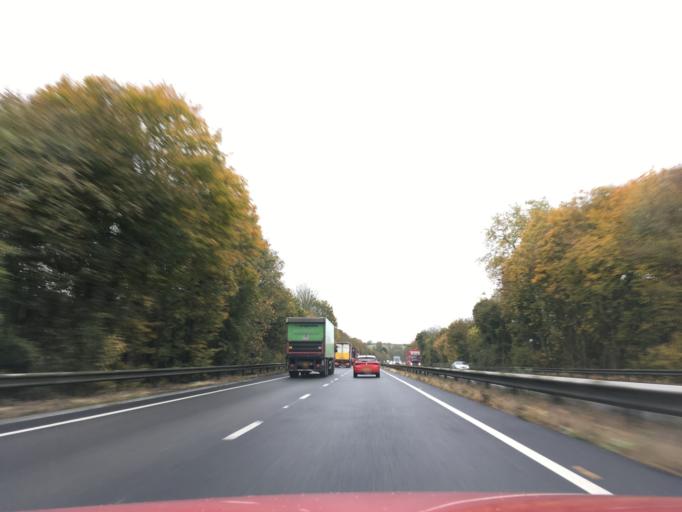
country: GB
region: England
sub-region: Hampshire
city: Overton
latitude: 51.2281
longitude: -1.3474
